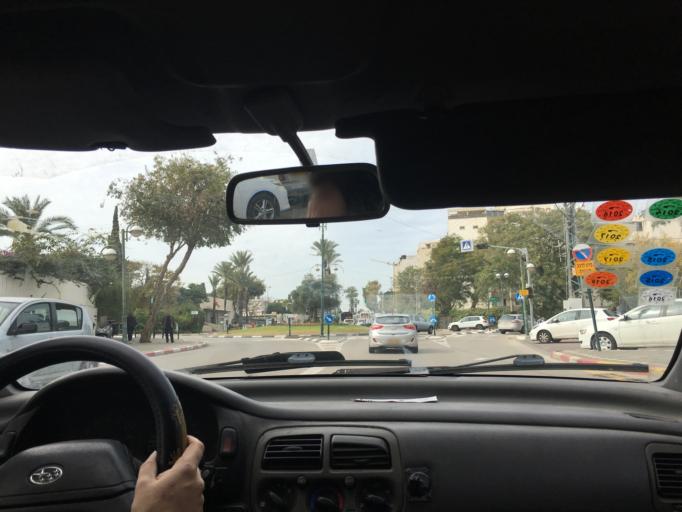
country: IL
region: Tel Aviv
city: Ramat HaSharon
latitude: 32.1368
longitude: 34.8434
